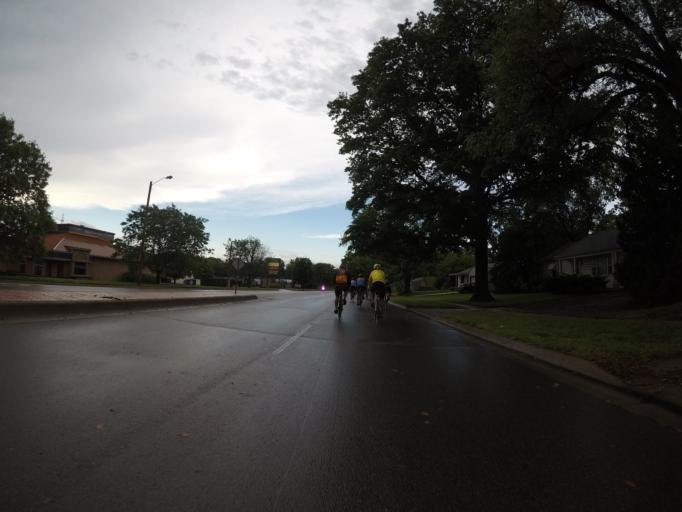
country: US
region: Kansas
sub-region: Shawnee County
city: Topeka
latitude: 39.0294
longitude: -95.6969
